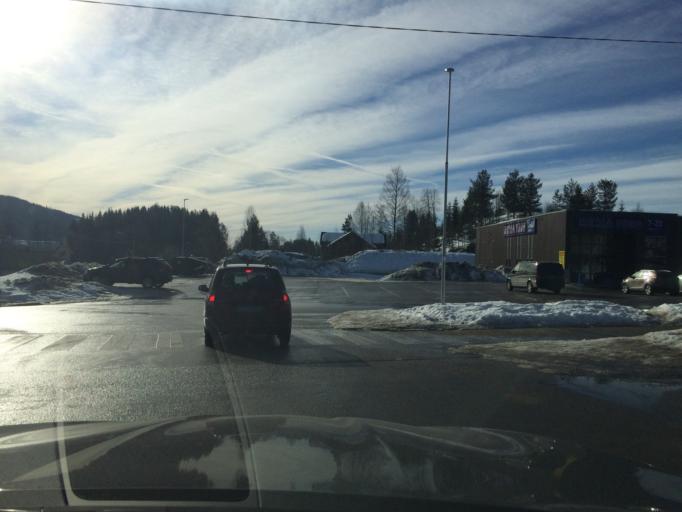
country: NO
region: Hedmark
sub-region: Trysil
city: Innbygda
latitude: 61.3150
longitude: 12.2559
